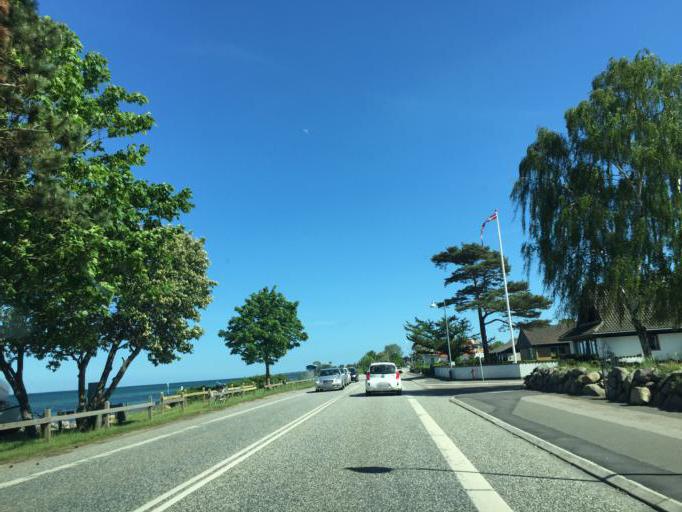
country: DK
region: Zealand
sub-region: Stevns Kommune
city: Stroby Egede
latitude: 55.4196
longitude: 12.2367
